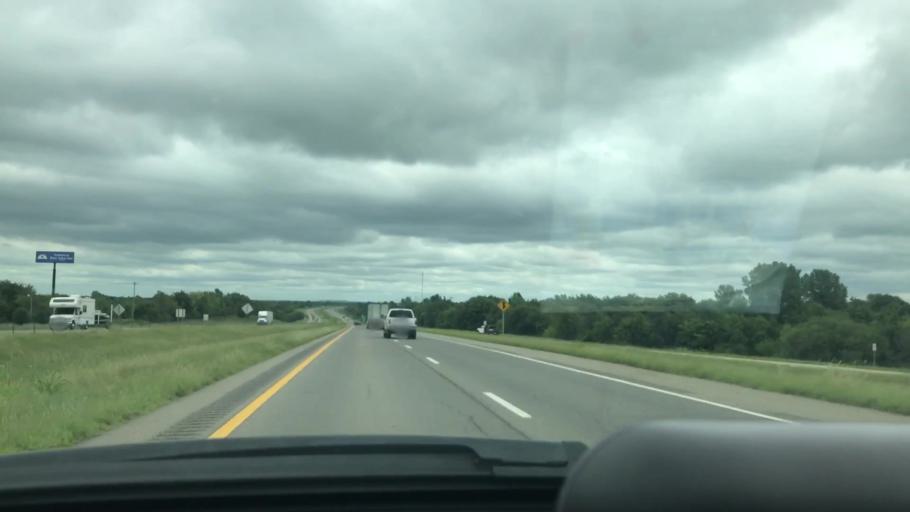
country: US
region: Oklahoma
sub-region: McIntosh County
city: Checotah
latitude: 35.4761
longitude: -95.5356
